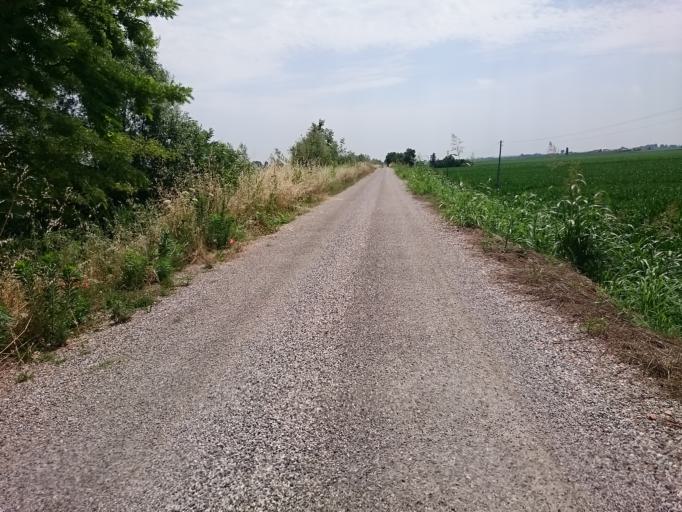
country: IT
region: Veneto
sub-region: Provincia di Venezia
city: Valli
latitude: 45.2167
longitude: 12.1608
